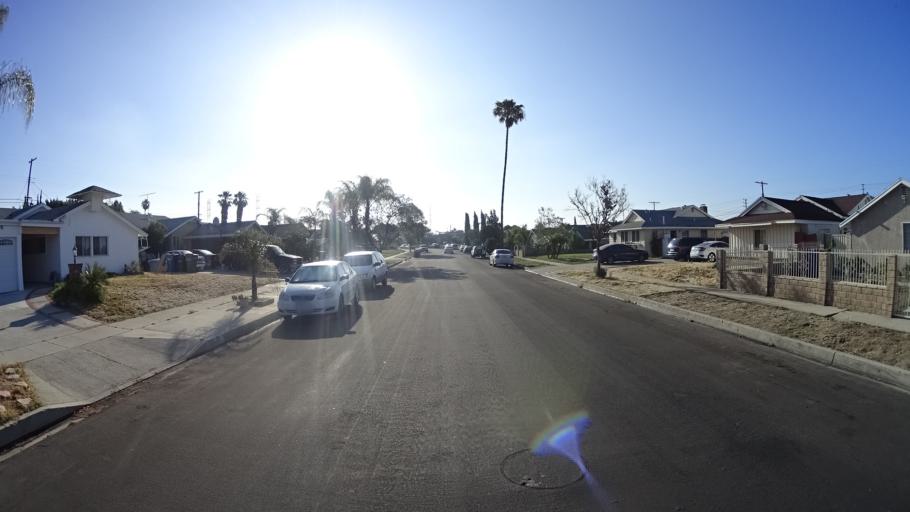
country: US
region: California
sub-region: Los Angeles County
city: Van Nuys
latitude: 34.2225
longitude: -118.4197
